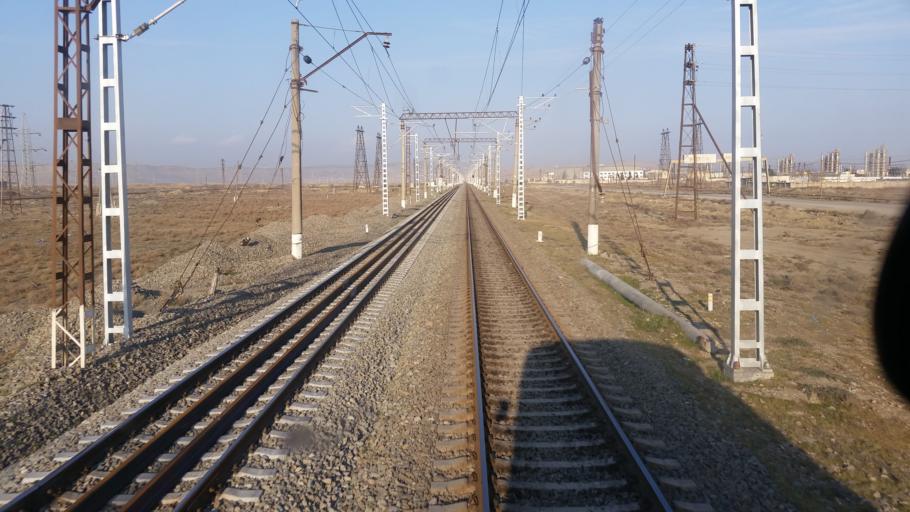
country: AZ
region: Baki
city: Puta
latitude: 40.2788
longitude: 49.6657
